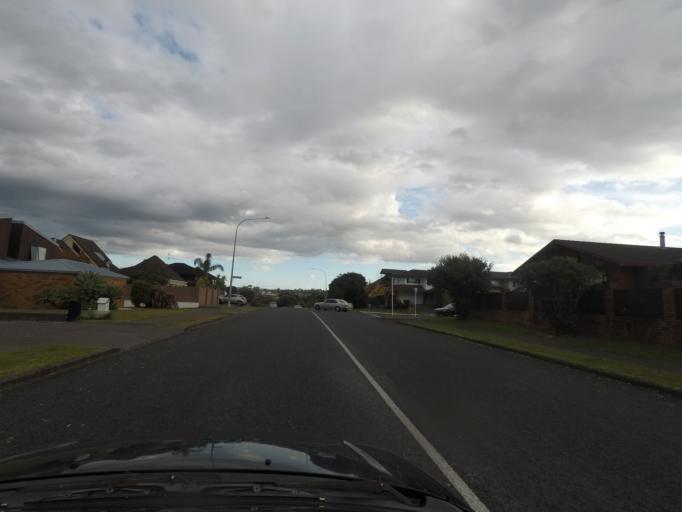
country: NZ
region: Auckland
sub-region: Auckland
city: Rosebank
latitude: -36.8050
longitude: 174.6428
